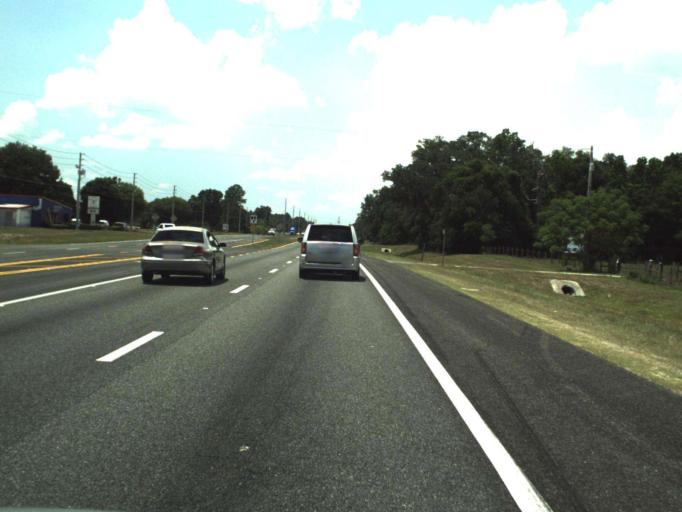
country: US
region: Florida
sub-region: Lake County
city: Leesburg
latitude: 28.8129
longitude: -81.9297
